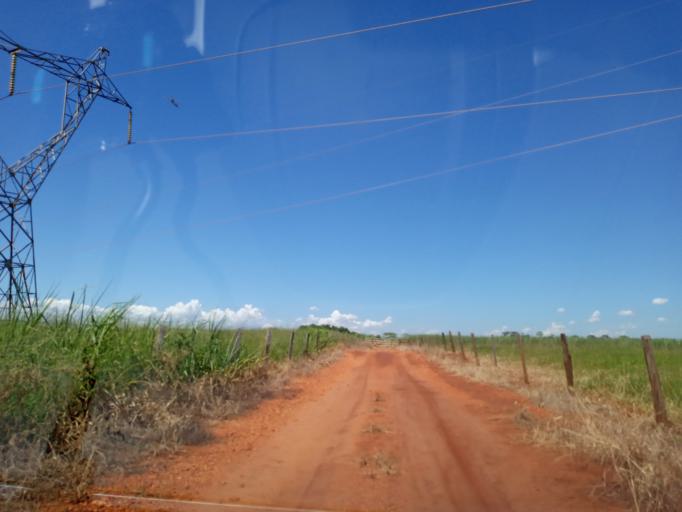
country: BR
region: Goias
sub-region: Itumbiara
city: Itumbiara
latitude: -18.4015
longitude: -49.1214
